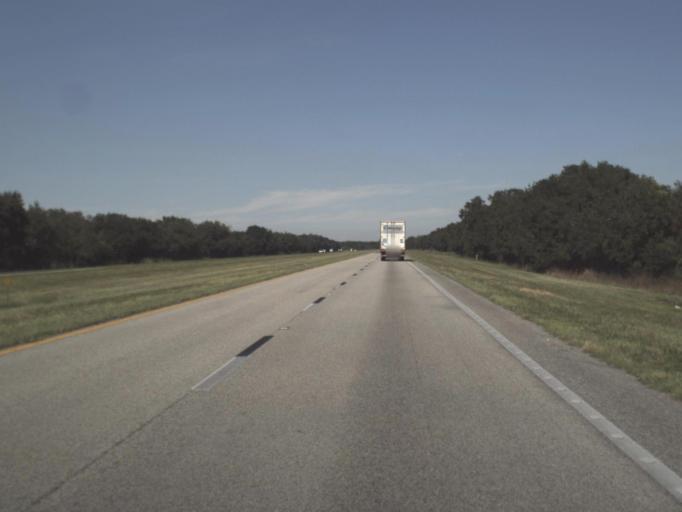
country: US
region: Florida
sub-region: Hendry County
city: Port LaBelle
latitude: 26.9601
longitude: -81.3164
